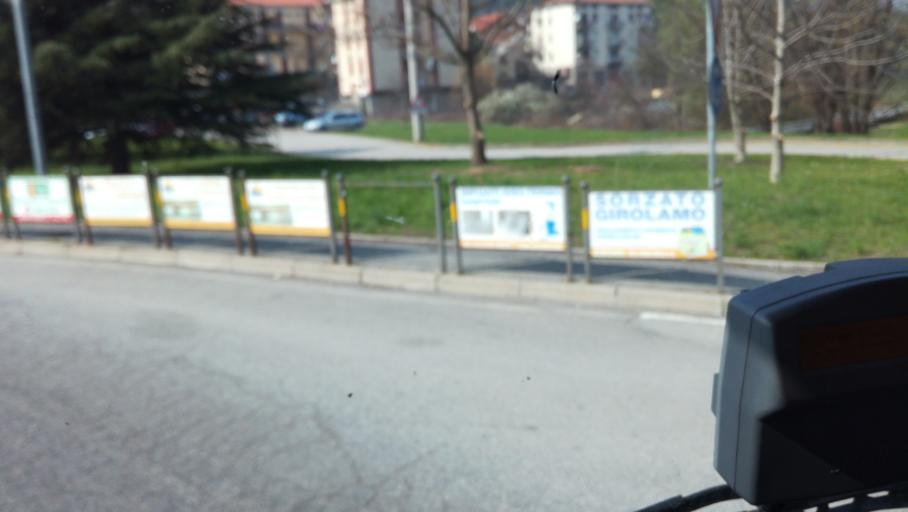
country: IT
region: Lombardy
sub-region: Provincia di Varese
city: Solbiate Arno
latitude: 45.7201
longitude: 8.8084
